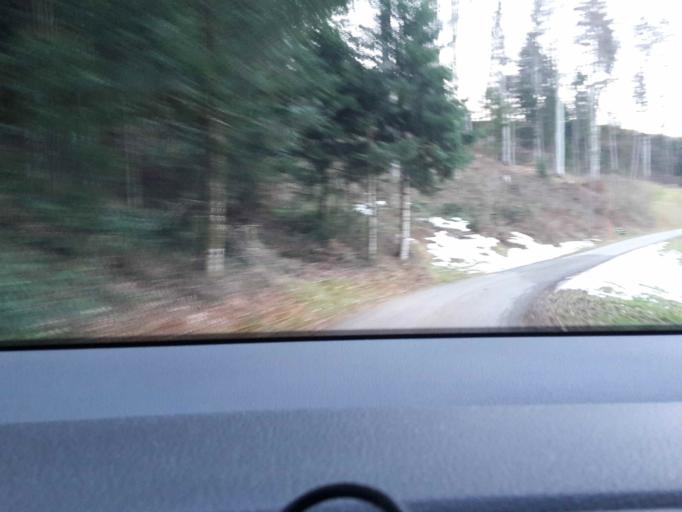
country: CH
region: Bern
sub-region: Oberaargau
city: Rohrbach
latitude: 47.1243
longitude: 7.7954
